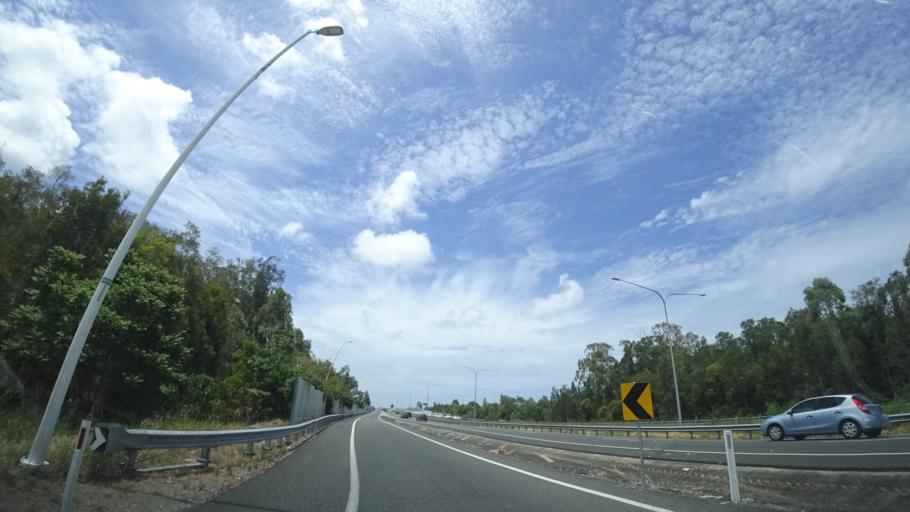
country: AU
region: Queensland
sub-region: Sunshine Coast
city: Buderim
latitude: -26.6463
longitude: 153.0663
